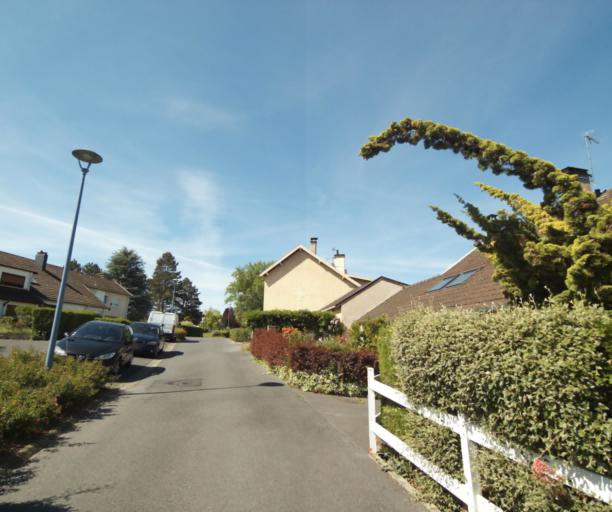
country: FR
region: Champagne-Ardenne
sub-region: Departement des Ardennes
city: La Francheville
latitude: 49.7442
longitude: 4.7173
